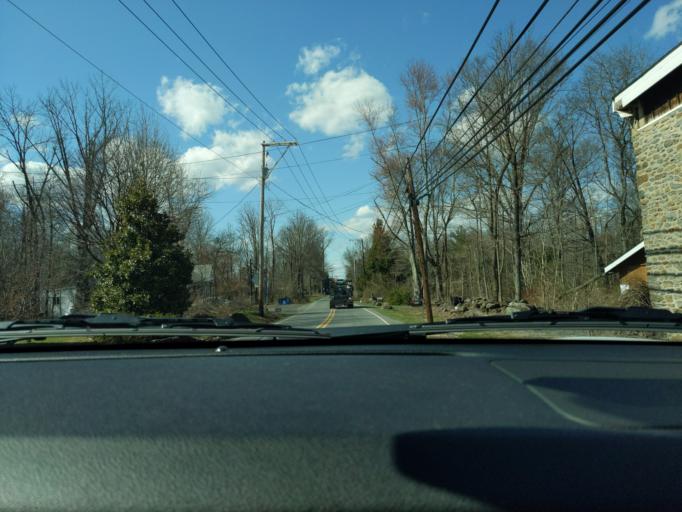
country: US
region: Pennsylvania
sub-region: Bucks County
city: Richlandtown
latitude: 40.4552
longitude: -75.2628
